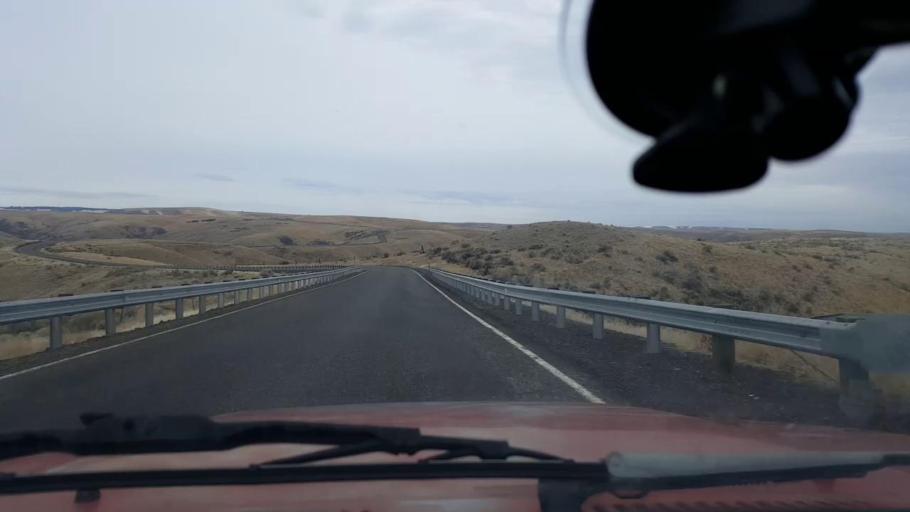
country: US
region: Washington
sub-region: Asotin County
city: Clarkston Heights-Vineland
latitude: 46.3347
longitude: -117.2855
